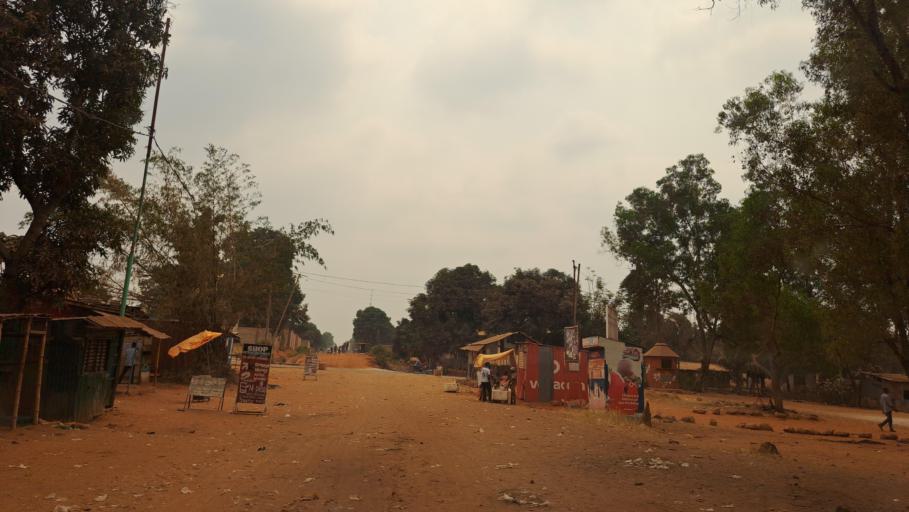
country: CD
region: Kasai-Oriental
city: Mbuji-Mayi
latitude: -6.1135
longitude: 23.5990
